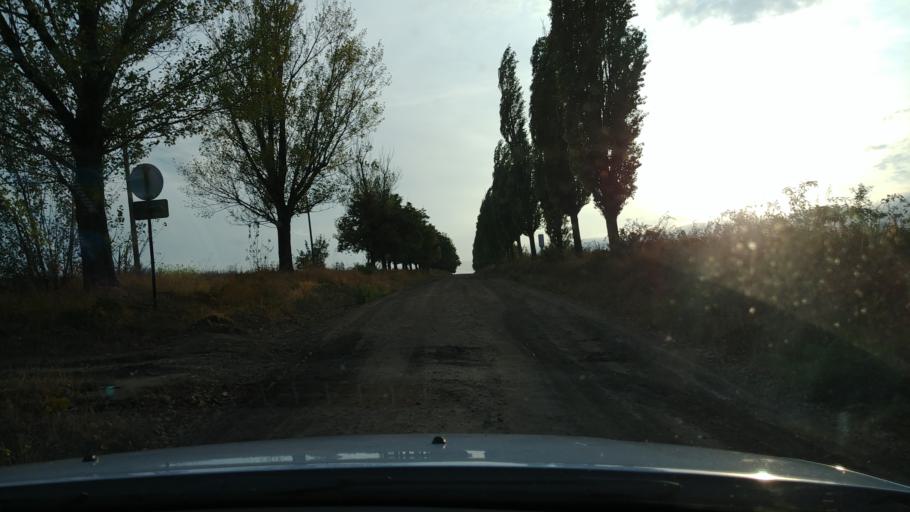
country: MD
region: Rezina
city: Saharna
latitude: 47.6801
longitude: 28.9699
